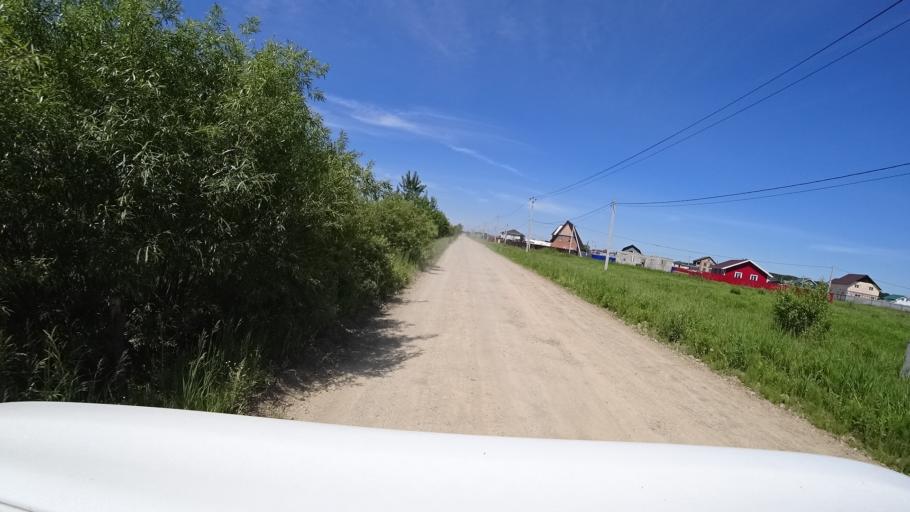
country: RU
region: Khabarovsk Krai
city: Topolevo
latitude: 48.5102
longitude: 135.1995
